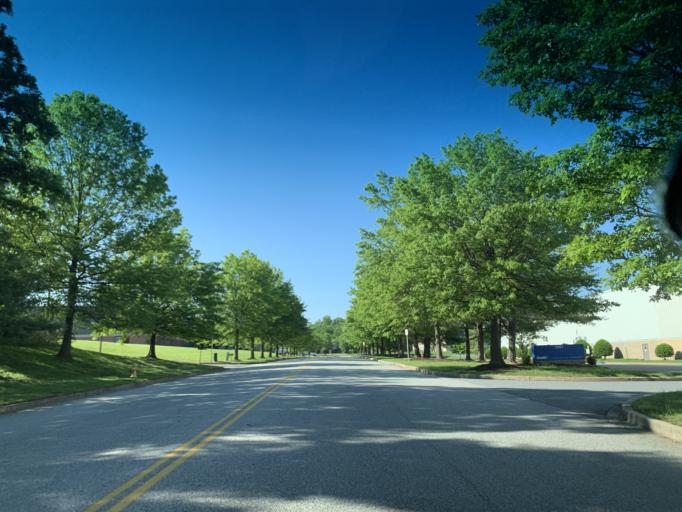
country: US
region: Maryland
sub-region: Harford County
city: Riverside
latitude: 39.4817
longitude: -76.2350
